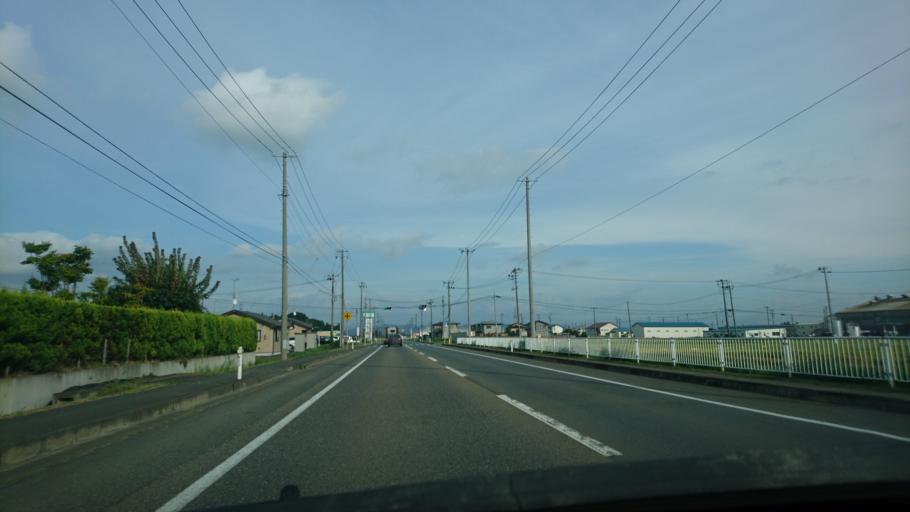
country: JP
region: Iwate
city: Kitakami
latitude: 39.3043
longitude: 141.0369
